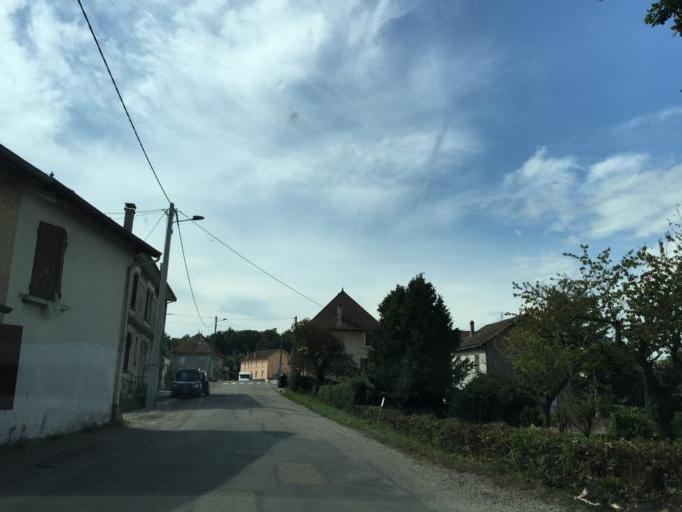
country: FR
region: Rhone-Alpes
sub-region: Departement de l'Isere
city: Saint-Andre-le-Gaz
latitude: 45.5437
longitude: 5.5262
